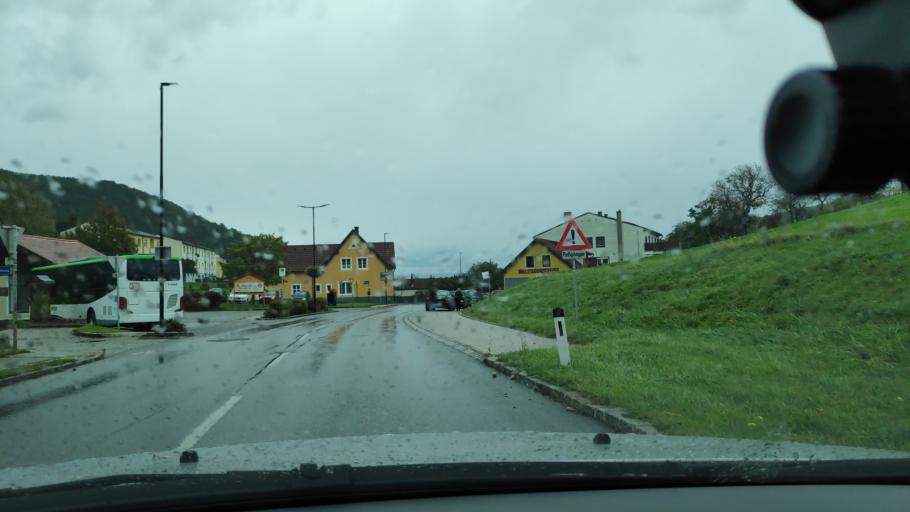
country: AT
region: Lower Austria
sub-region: Politischer Bezirk Neunkirchen
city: Willendorf am Steinfelde
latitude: 47.7948
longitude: 16.0365
